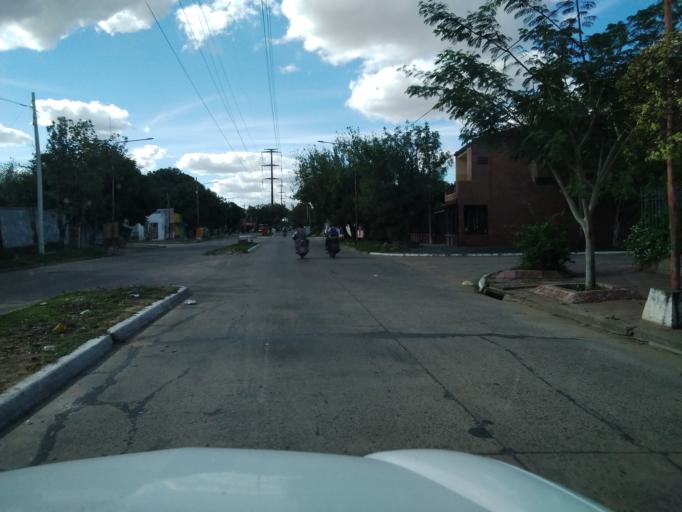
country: AR
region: Corrientes
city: Corrientes
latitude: -27.4922
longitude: -58.8380
